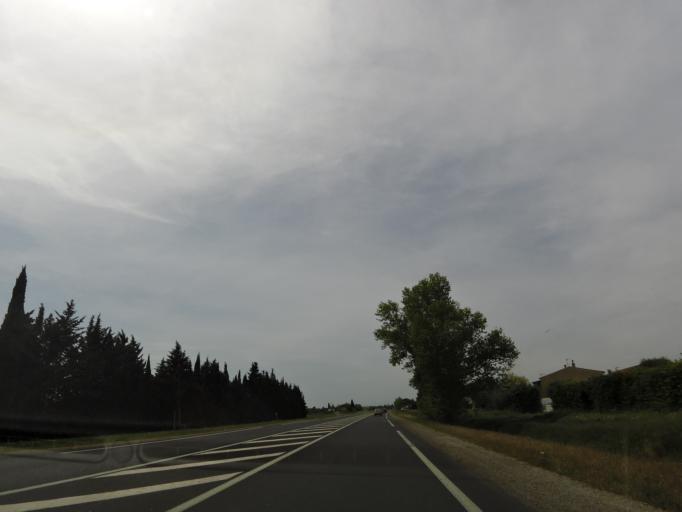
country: FR
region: Languedoc-Roussillon
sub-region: Departement de l'Herault
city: Lunel
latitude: 43.6706
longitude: 4.1453
